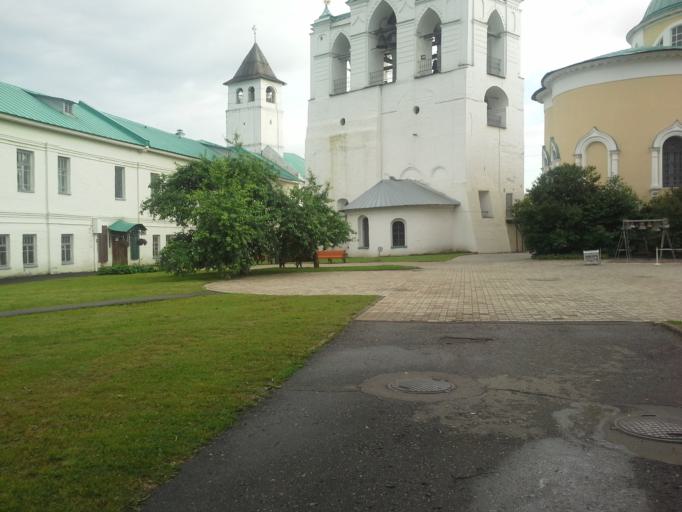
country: RU
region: Jaroslavl
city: Yaroslavl
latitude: 57.6217
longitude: 39.8904
